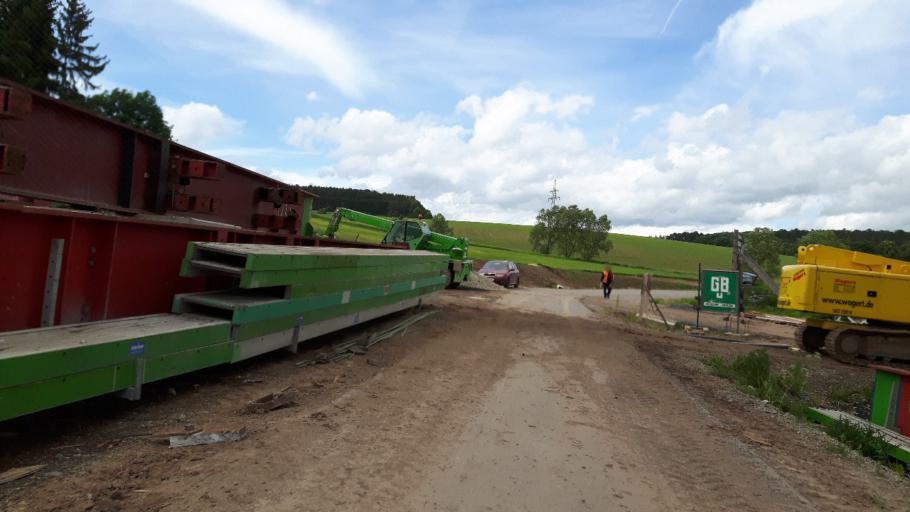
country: DE
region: Thuringia
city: Behringen
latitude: 50.7608
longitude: 11.0481
